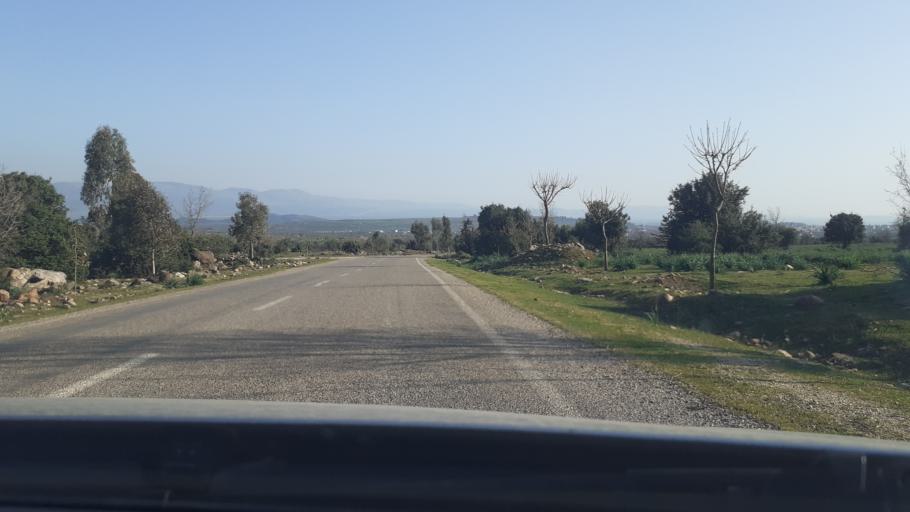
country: TR
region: Hatay
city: Aktepe
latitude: 36.7264
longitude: 36.4842
